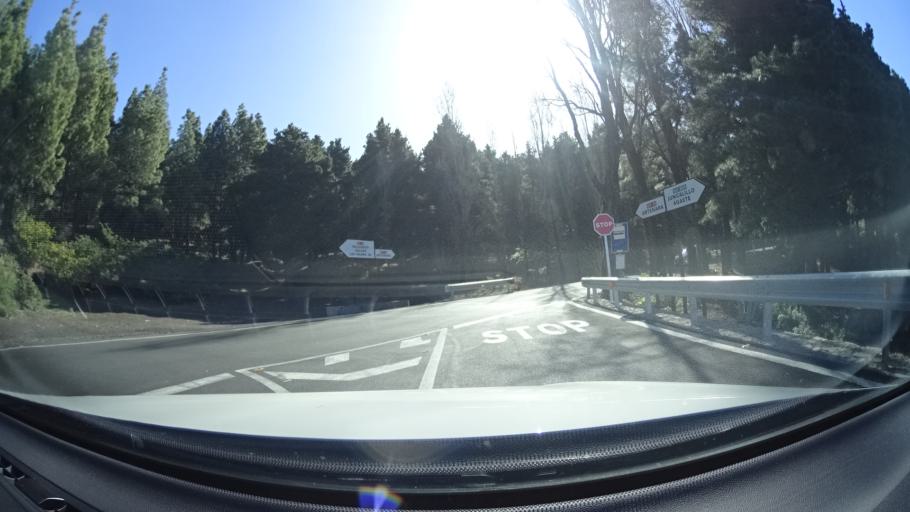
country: ES
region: Canary Islands
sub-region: Provincia de Las Palmas
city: Artenara
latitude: 28.0312
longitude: -15.6215
